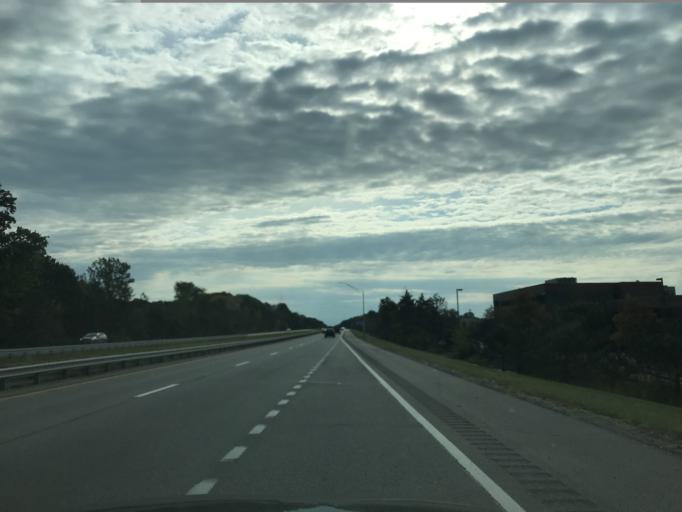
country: US
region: Ohio
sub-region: Cuyahoga County
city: Solon
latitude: 41.4026
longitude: -81.4620
